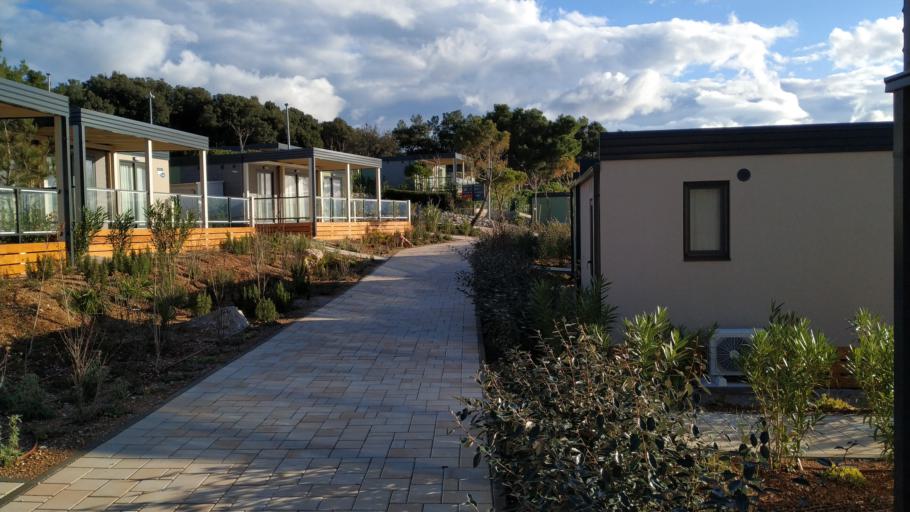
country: HR
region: Primorsko-Goranska
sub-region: Grad Krk
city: Krk
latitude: 45.0181
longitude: 14.5673
